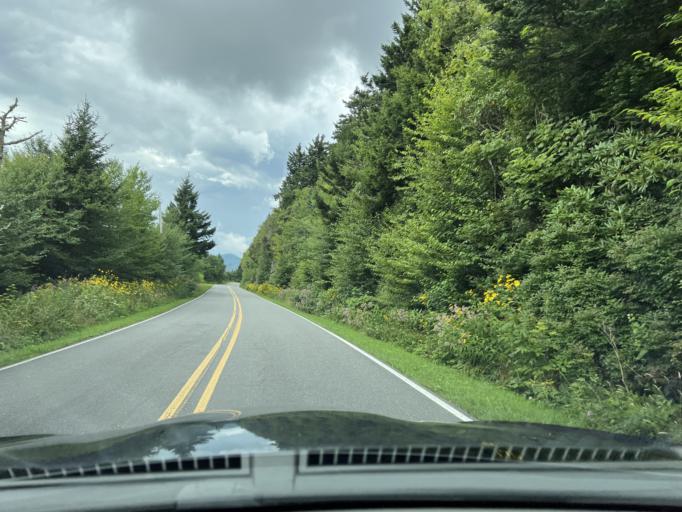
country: US
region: North Carolina
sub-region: Buncombe County
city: Black Mountain
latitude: 35.7436
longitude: -82.2780
